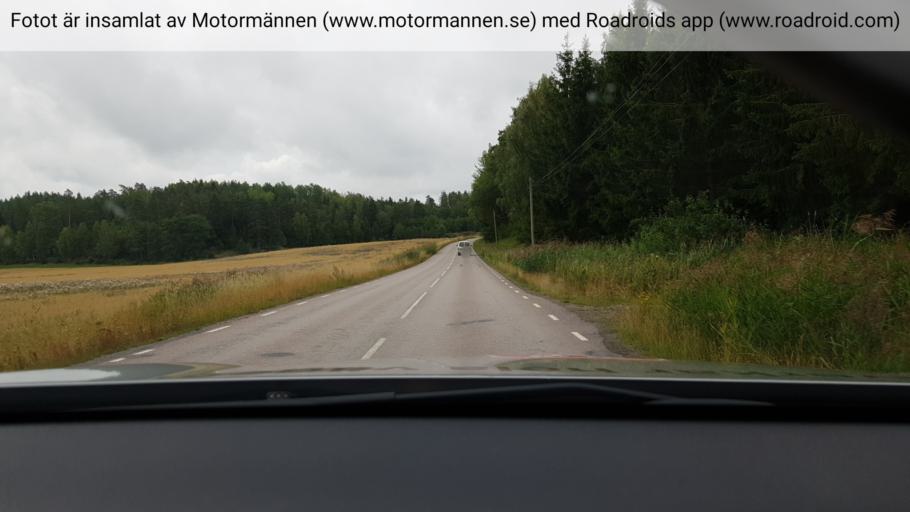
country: SE
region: Soedermanland
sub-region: Gnesta Kommun
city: Gnesta
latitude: 59.0926
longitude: 17.2501
